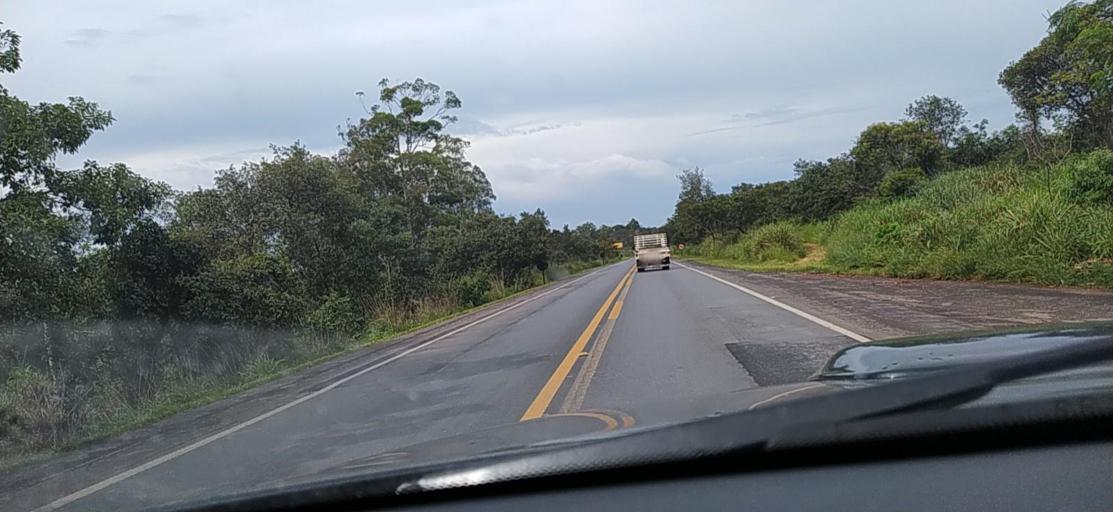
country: BR
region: Minas Gerais
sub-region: Montes Claros
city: Montes Claros
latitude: -16.8744
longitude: -43.8586
